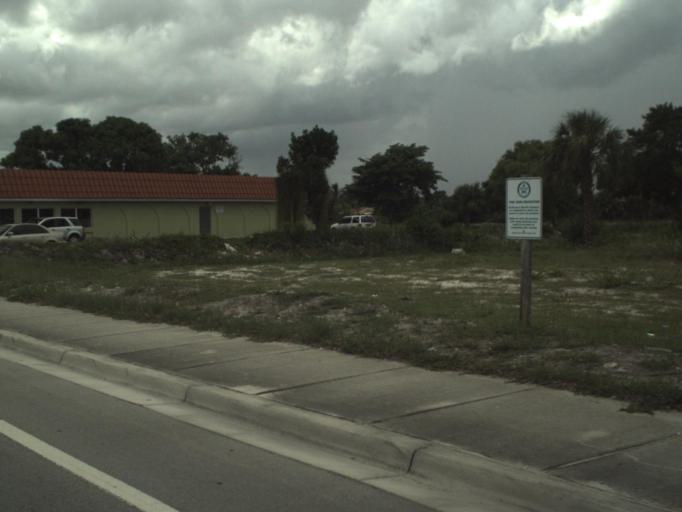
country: US
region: Florida
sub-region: Broward County
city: Pompano Beach Highlands
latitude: 26.2710
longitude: -80.1150
